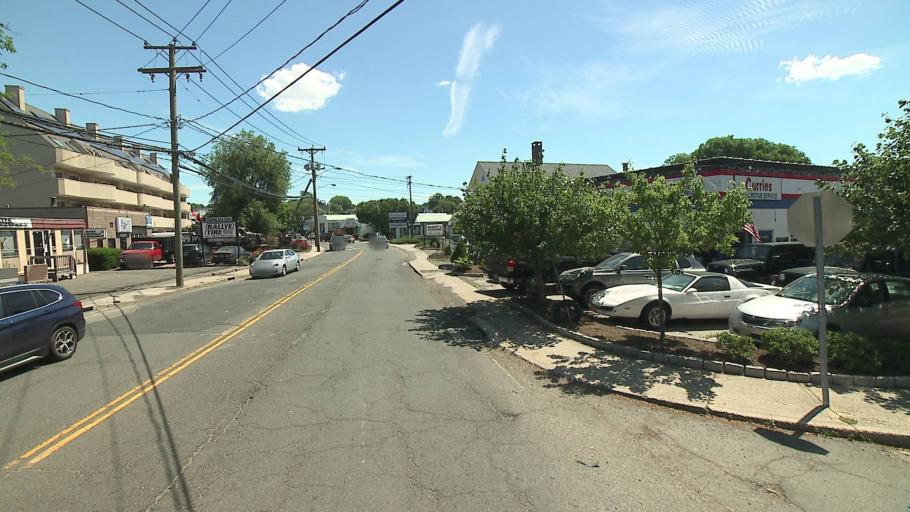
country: US
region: Connecticut
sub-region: Fairfield County
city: Norwalk
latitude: 41.1201
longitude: -73.4156
